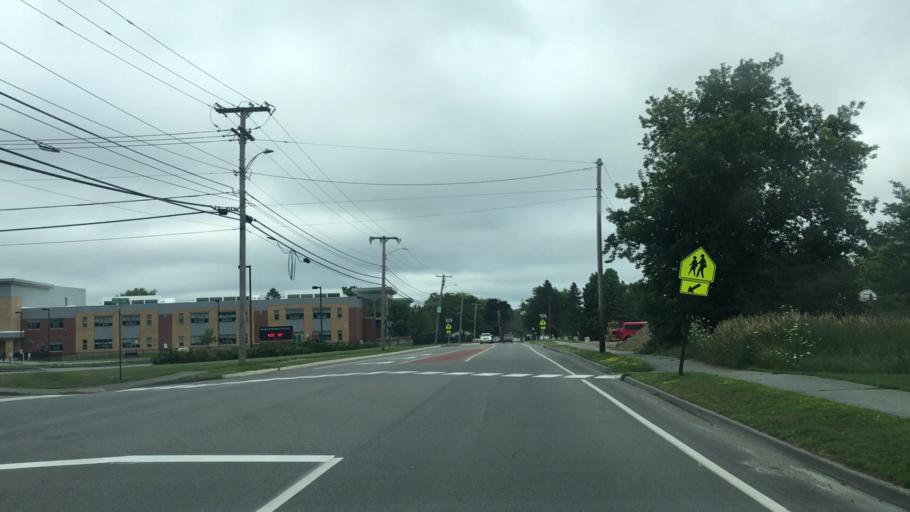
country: US
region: Maine
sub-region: Penobscot County
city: Brewer
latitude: 44.7749
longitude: -68.7698
